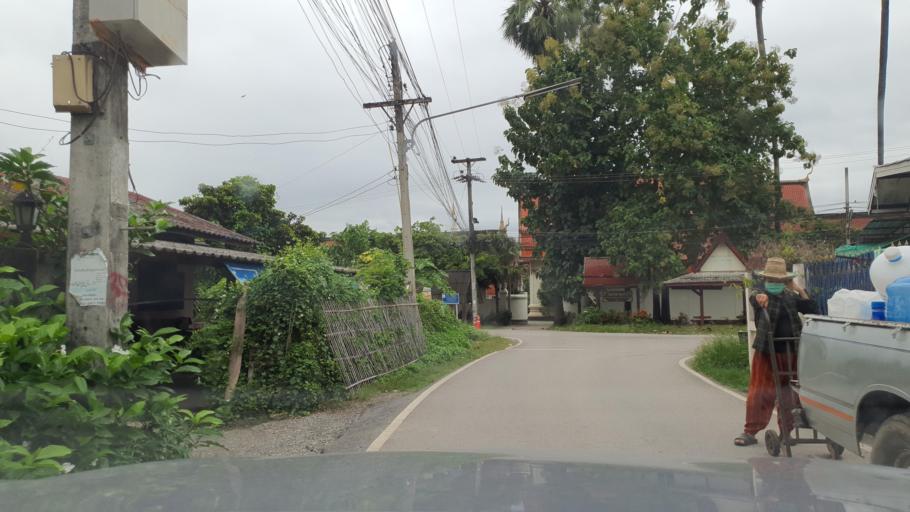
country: TH
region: Lamphun
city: Lamphun
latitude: 18.6001
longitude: 98.9731
